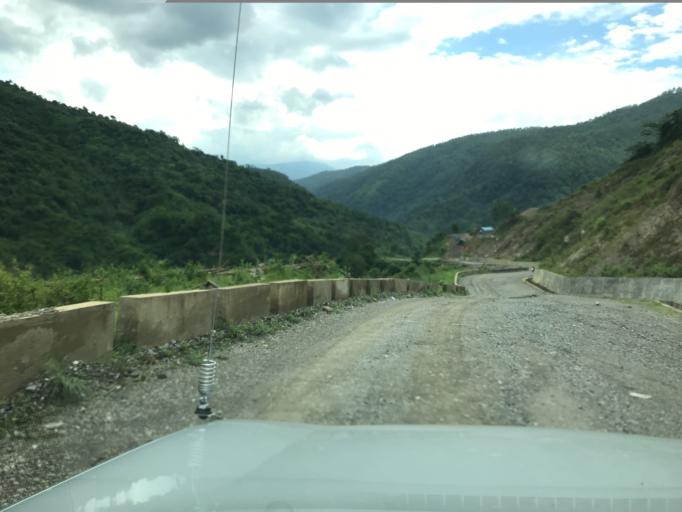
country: TL
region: Aileu
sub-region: Aileu Villa
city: Aileu
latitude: -8.6428
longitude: 125.5151
